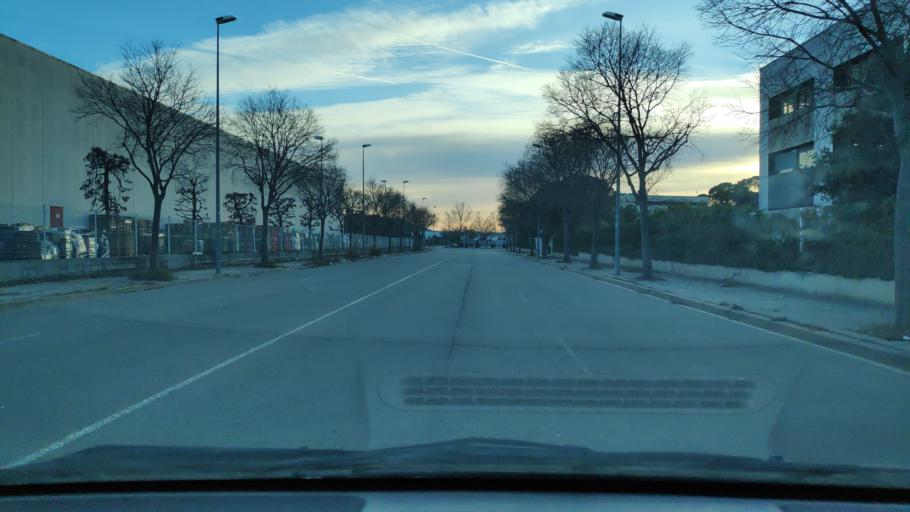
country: ES
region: Catalonia
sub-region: Provincia de Barcelona
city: Montmelo
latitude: 41.5678
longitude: 2.2650
